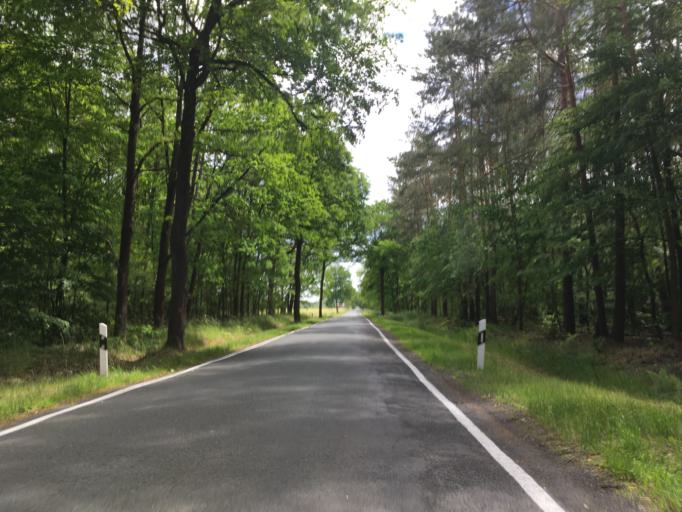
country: DE
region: Brandenburg
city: Melchow
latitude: 52.7369
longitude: 13.7420
